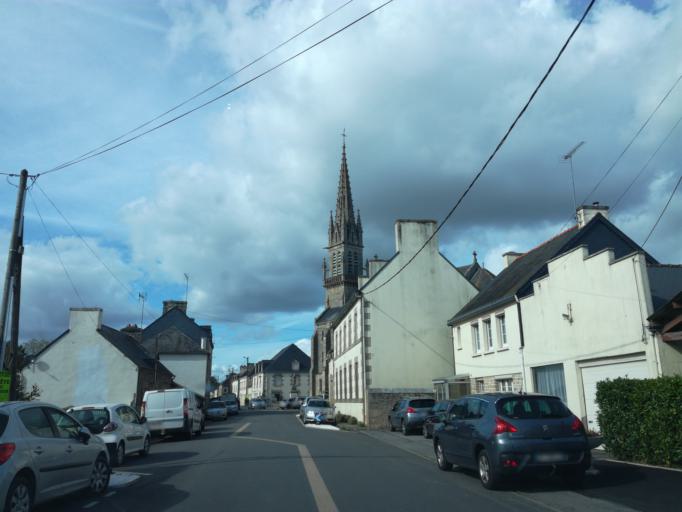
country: FR
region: Brittany
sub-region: Departement du Morbihan
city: Rohan
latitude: 48.0860
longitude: -2.7658
